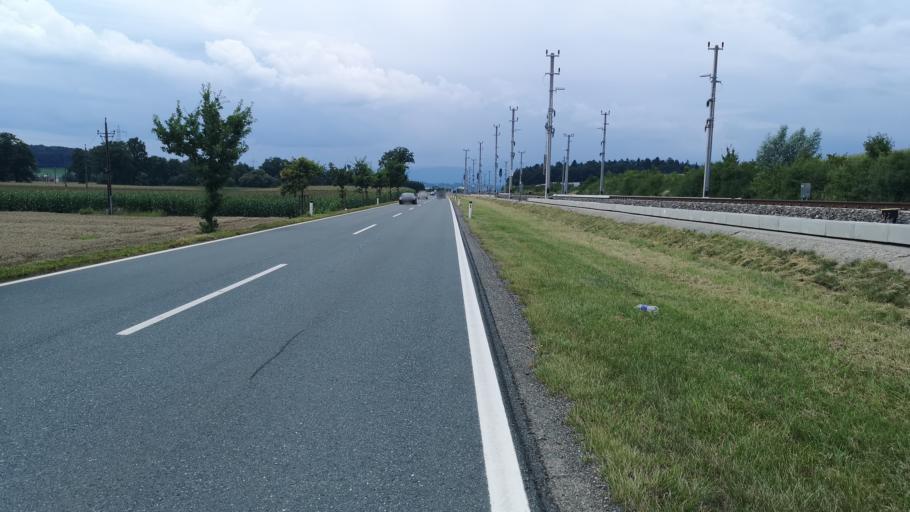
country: AT
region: Styria
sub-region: Politischer Bezirk Deutschlandsberg
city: Wettmannstatten
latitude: 46.8409
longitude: 15.3914
